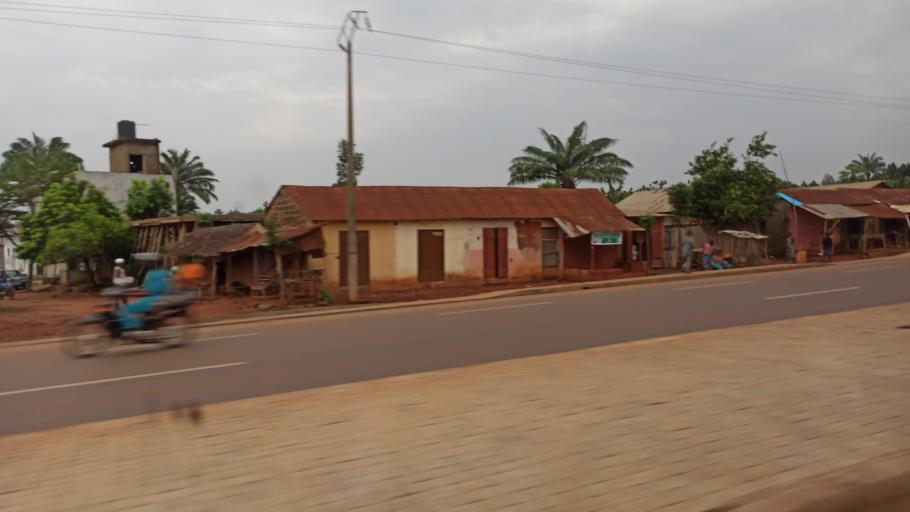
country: BJ
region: Queme
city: Porto-Novo
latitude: 6.5335
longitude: 2.5981
